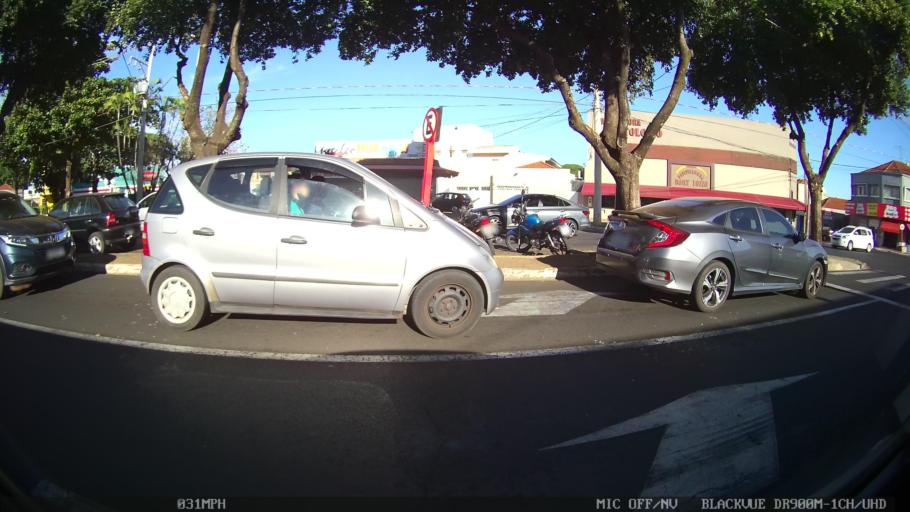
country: BR
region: Sao Paulo
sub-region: Araraquara
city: Araraquara
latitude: -21.7790
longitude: -48.1792
